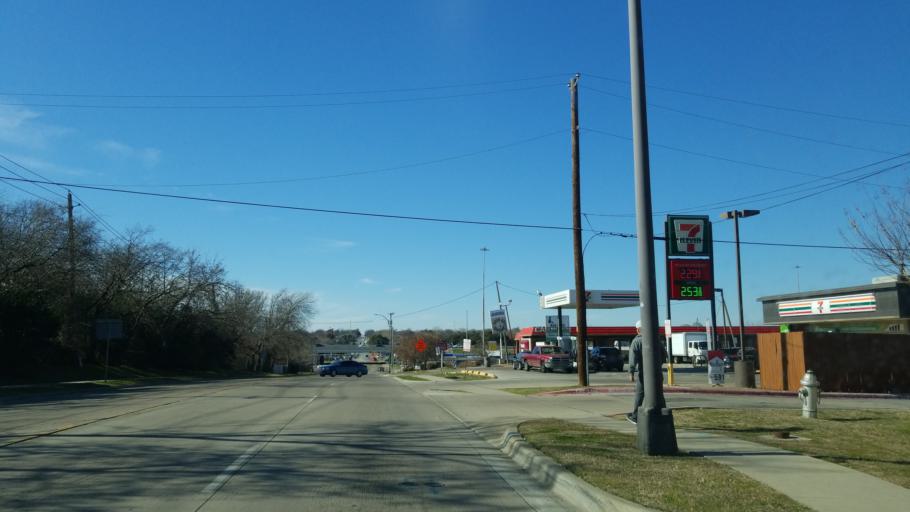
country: US
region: Texas
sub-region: Tarrant County
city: Arlington
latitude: 32.7208
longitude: -97.0590
